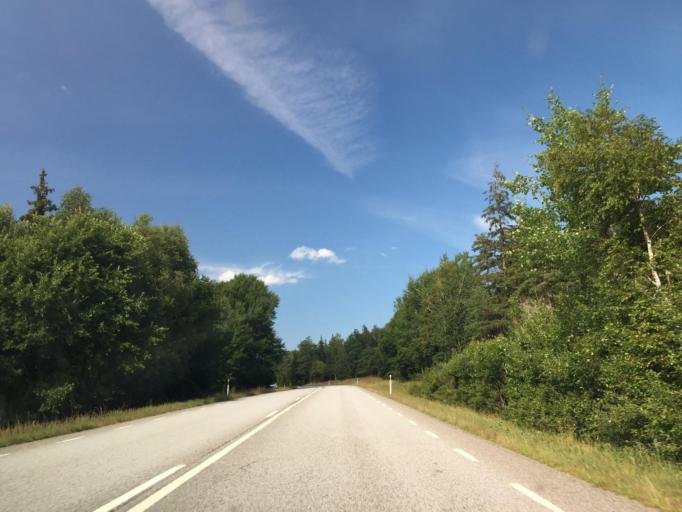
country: SE
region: Vaestra Goetaland
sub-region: Tanums Kommun
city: Tanumshede
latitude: 58.8160
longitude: 11.2629
